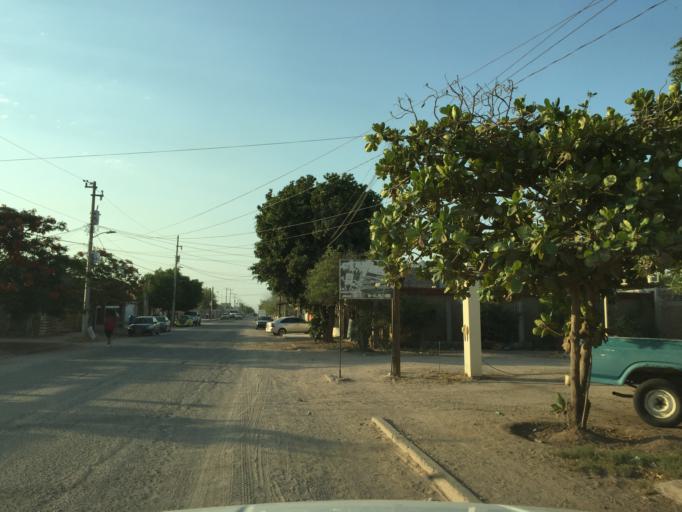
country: MX
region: Sonora
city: Navojoa
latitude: 27.0532
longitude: -109.4572
